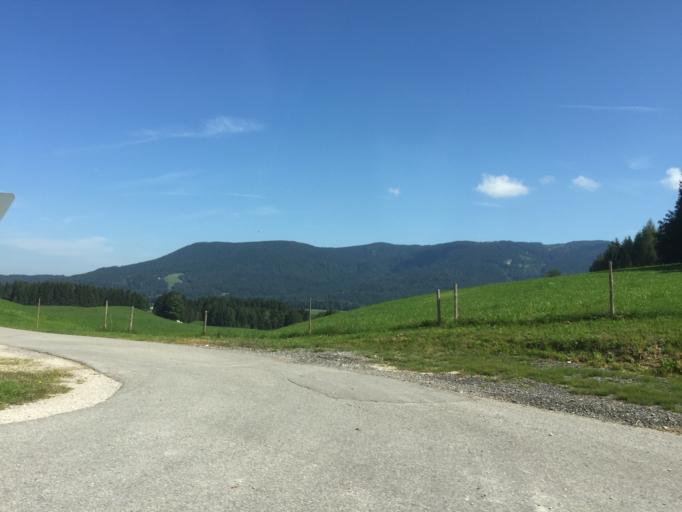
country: DE
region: Bavaria
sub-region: Upper Bavaria
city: Inzell
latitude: 47.7626
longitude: 12.7242
